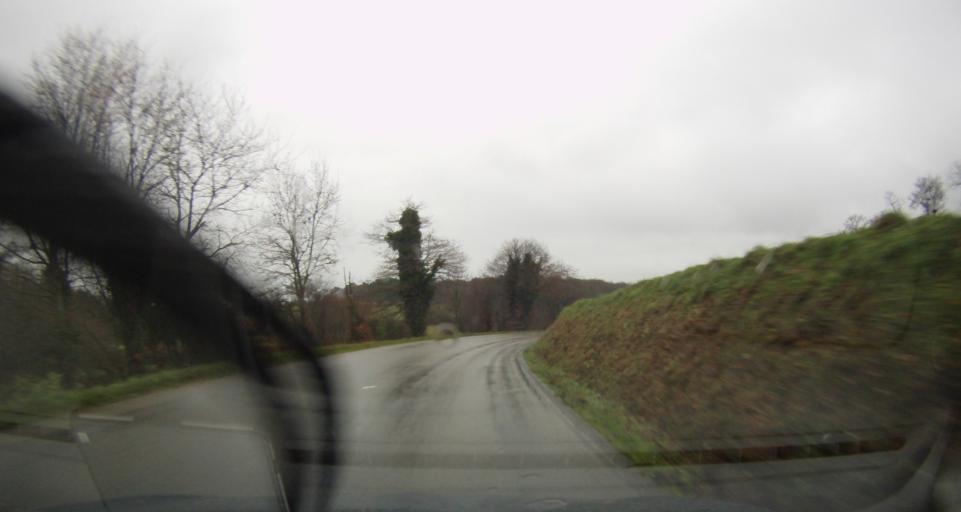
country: FR
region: Brittany
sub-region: Departement d'Ille-et-Vilaine
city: Chanteloup
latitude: 47.9430
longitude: -1.6267
